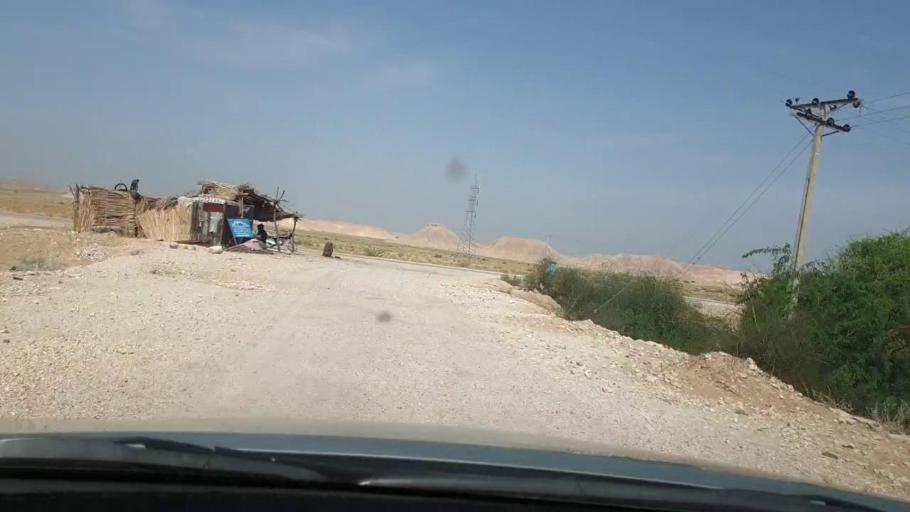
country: PK
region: Sindh
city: Kot Diji
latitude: 27.3282
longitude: 68.7927
